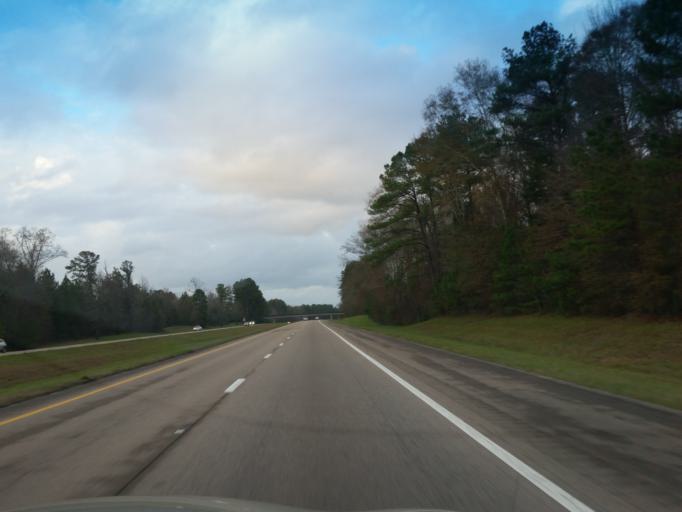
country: US
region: Mississippi
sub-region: Clarke County
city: Stonewall
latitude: 32.0335
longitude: -88.9216
